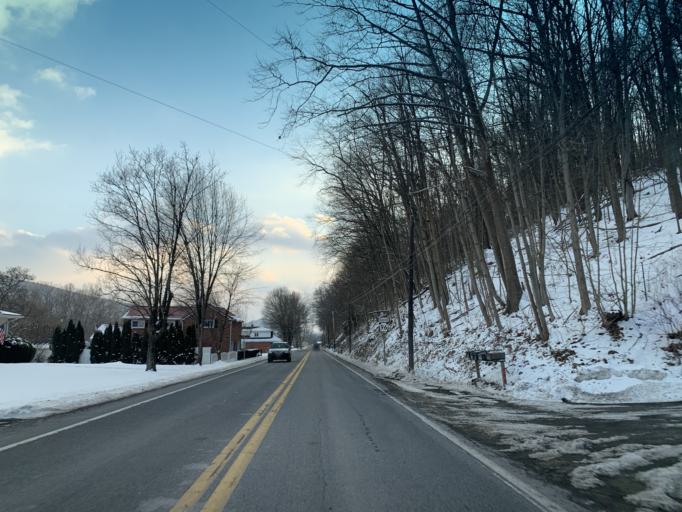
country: US
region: Maryland
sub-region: Allegany County
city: Cumberland
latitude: 39.7505
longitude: -78.7519
